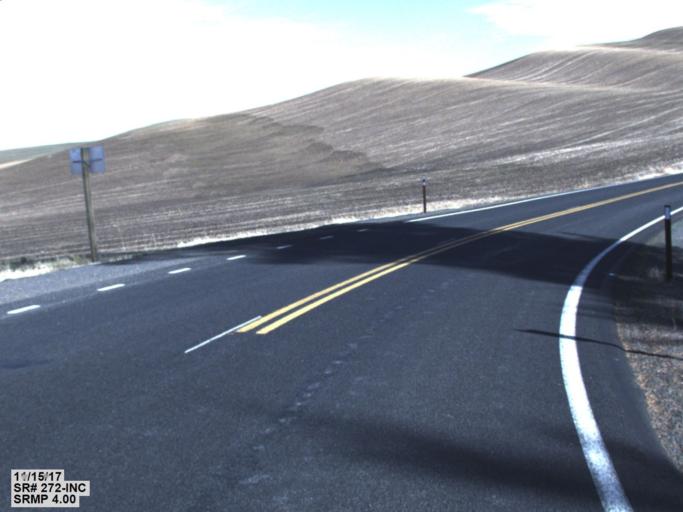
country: US
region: Washington
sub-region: Whitman County
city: Colfax
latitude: 46.9058
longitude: -117.2934
